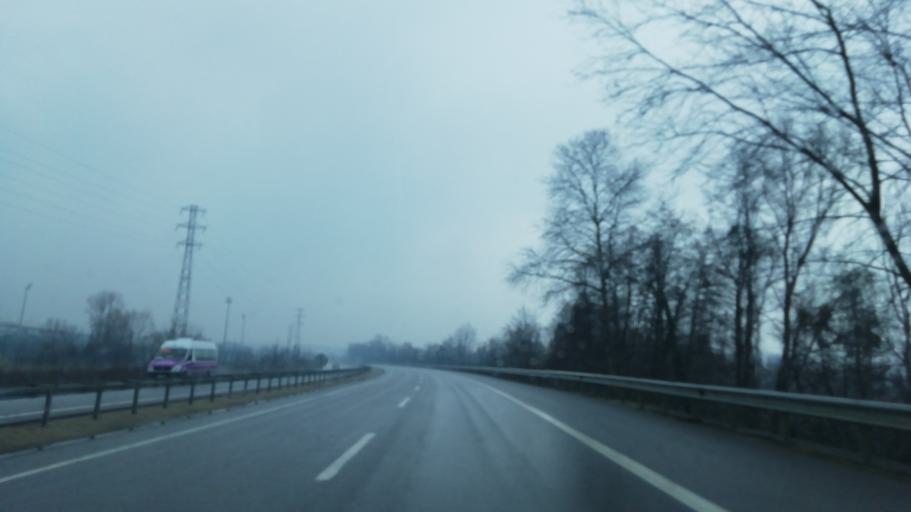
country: TR
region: Sakarya
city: Akyazi
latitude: 40.6704
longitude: 30.5884
